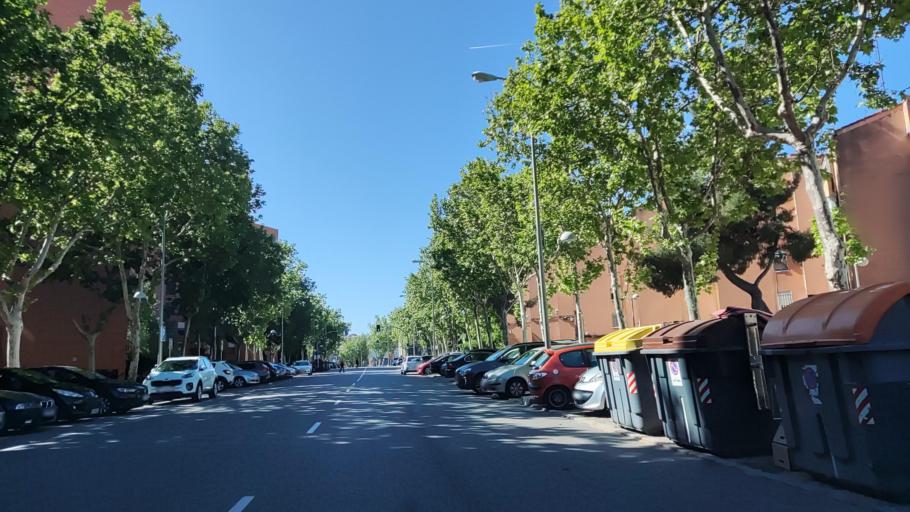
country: ES
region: Madrid
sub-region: Provincia de Madrid
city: San Blas
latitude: 40.4312
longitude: -3.6160
